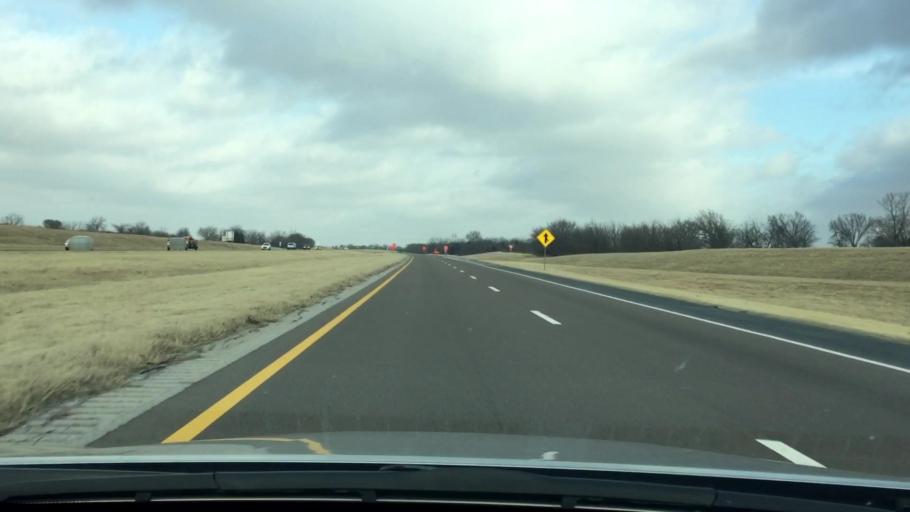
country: US
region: Oklahoma
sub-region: Garvin County
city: Maysville
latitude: 34.8280
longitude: -97.3096
